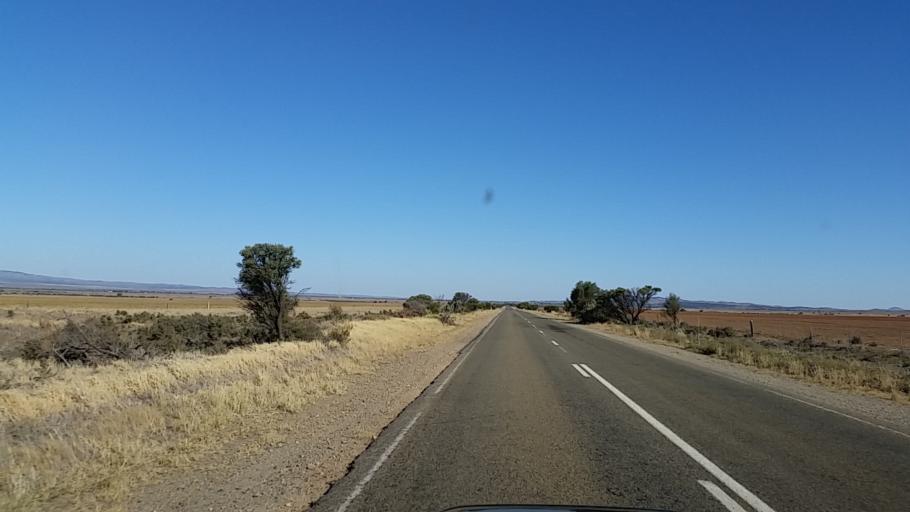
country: AU
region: South Australia
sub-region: Peterborough
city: Peterborough
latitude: -32.6505
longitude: 138.6015
